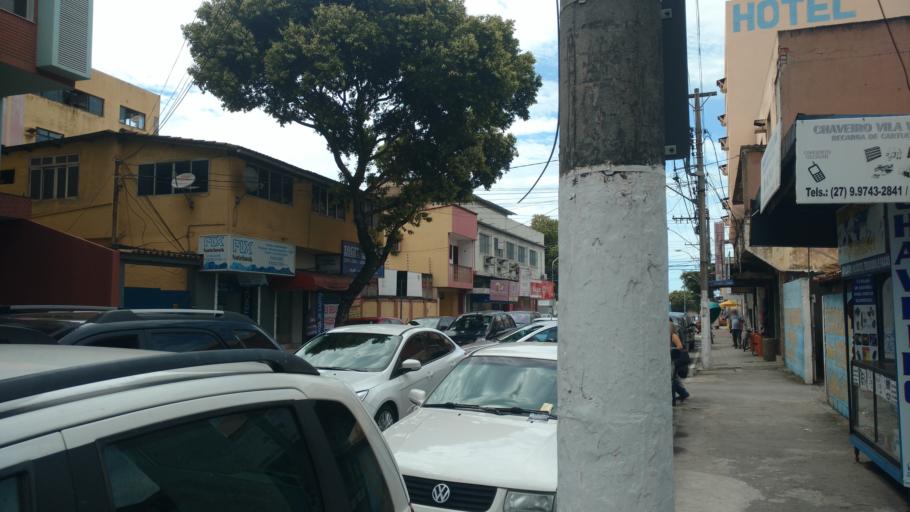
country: BR
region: Espirito Santo
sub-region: Vila Velha
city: Vila Velha
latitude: -20.3351
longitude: -40.2940
